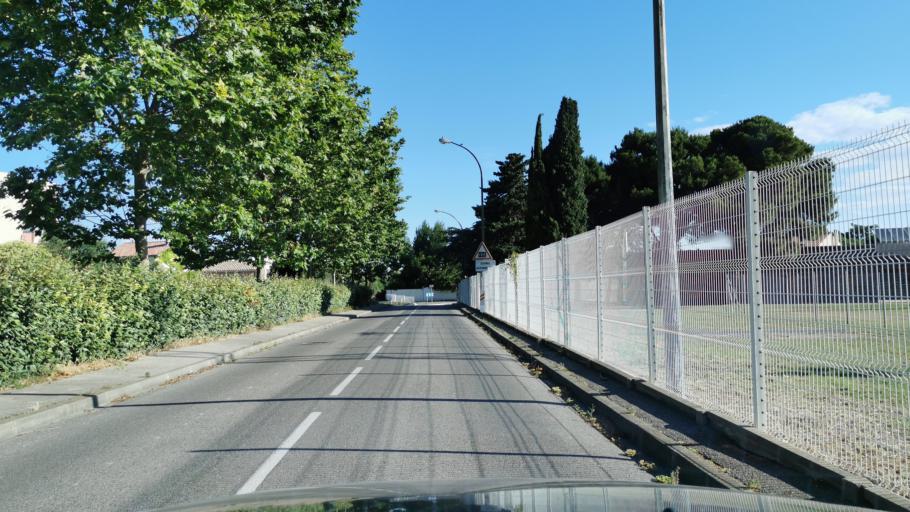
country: FR
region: Languedoc-Roussillon
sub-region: Departement de l'Aude
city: Narbonne
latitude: 43.1849
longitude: 2.9887
